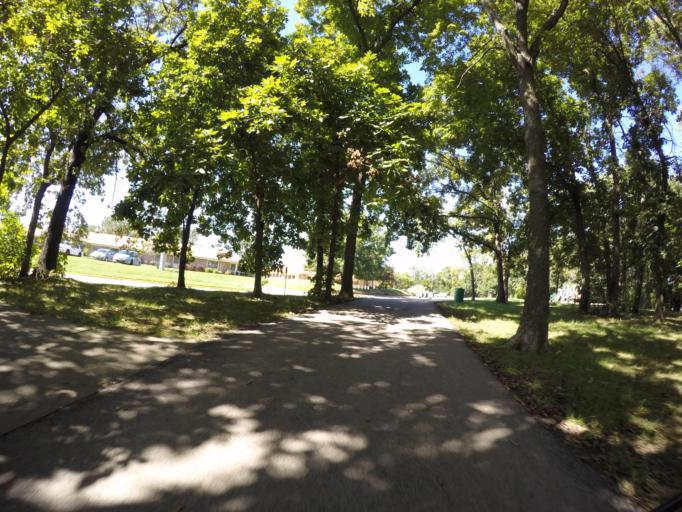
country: US
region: Kansas
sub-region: Johnson County
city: Overland Park
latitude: 38.9401
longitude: -94.6614
